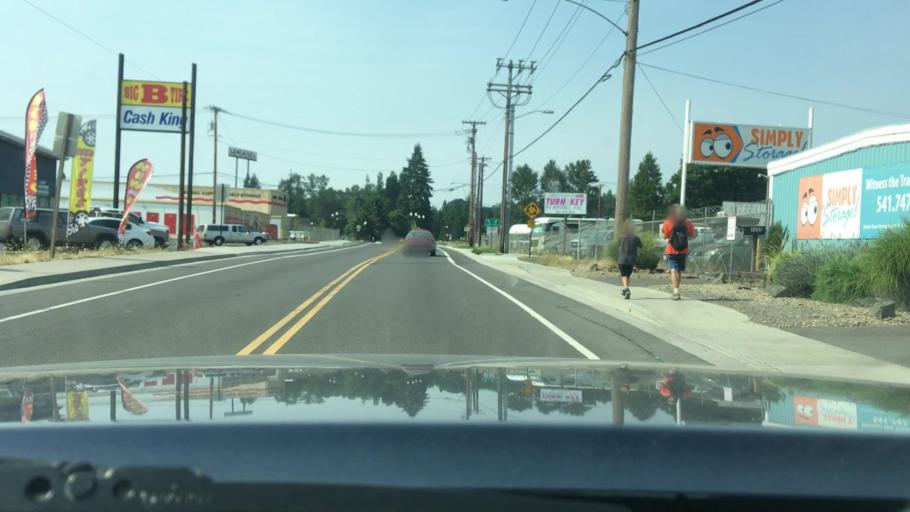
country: US
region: Oregon
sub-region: Lane County
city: Springfield
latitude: 44.0424
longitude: -123.0296
